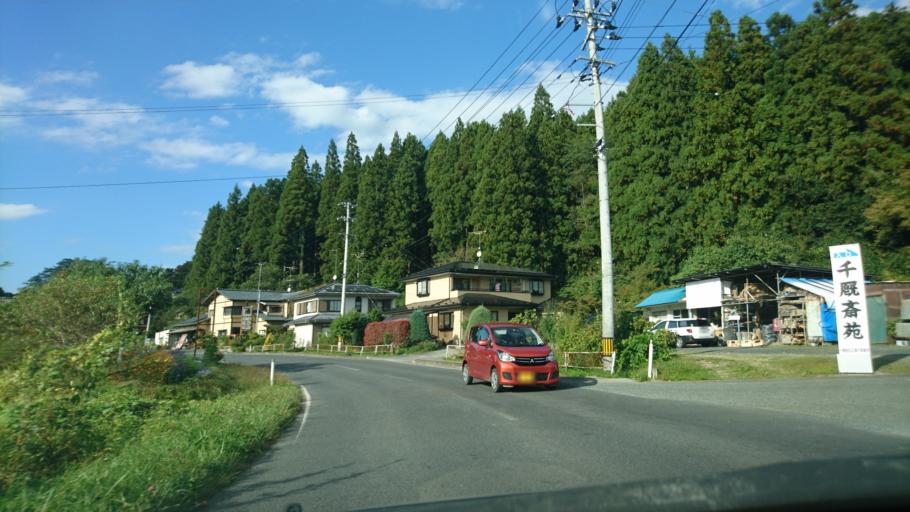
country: JP
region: Iwate
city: Ichinoseki
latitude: 38.9005
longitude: 141.3254
